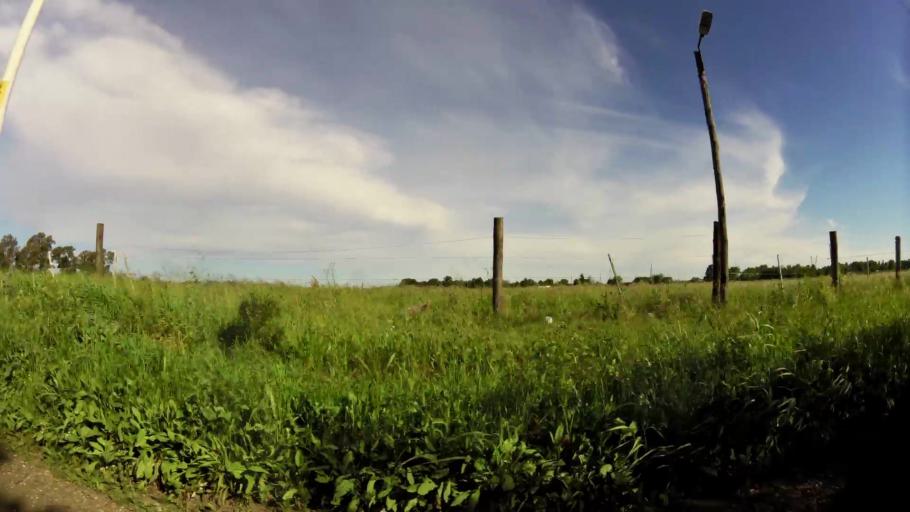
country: AR
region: Buenos Aires
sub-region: Partido de Almirante Brown
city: Adrogue
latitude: -34.8257
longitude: -58.3373
